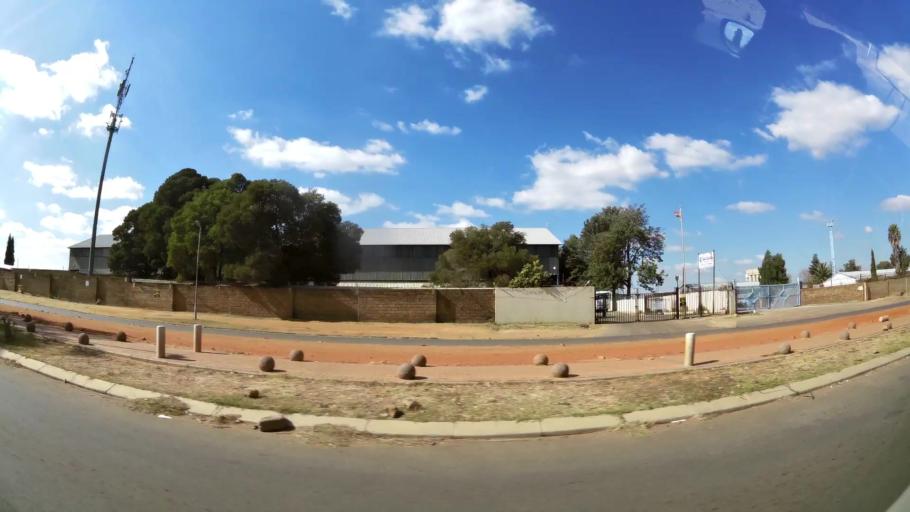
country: ZA
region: Gauteng
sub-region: West Rand District Municipality
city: Krugersdorp
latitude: -26.1470
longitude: 27.7899
